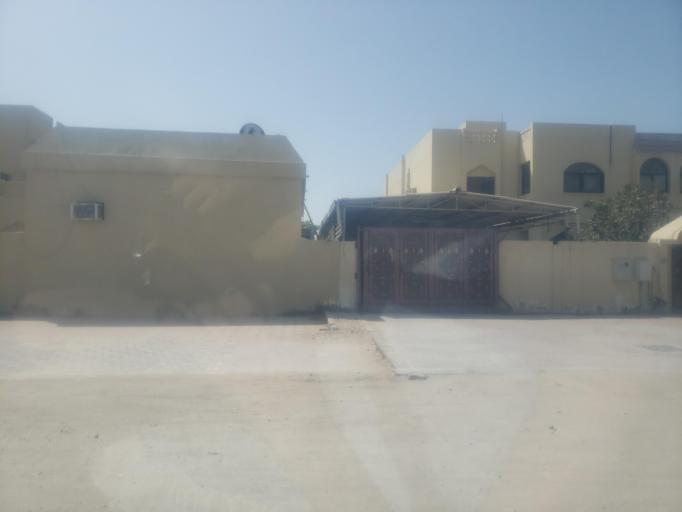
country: AE
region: Ra's al Khaymah
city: Ras al-Khaimah
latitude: 25.8031
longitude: 55.9606
